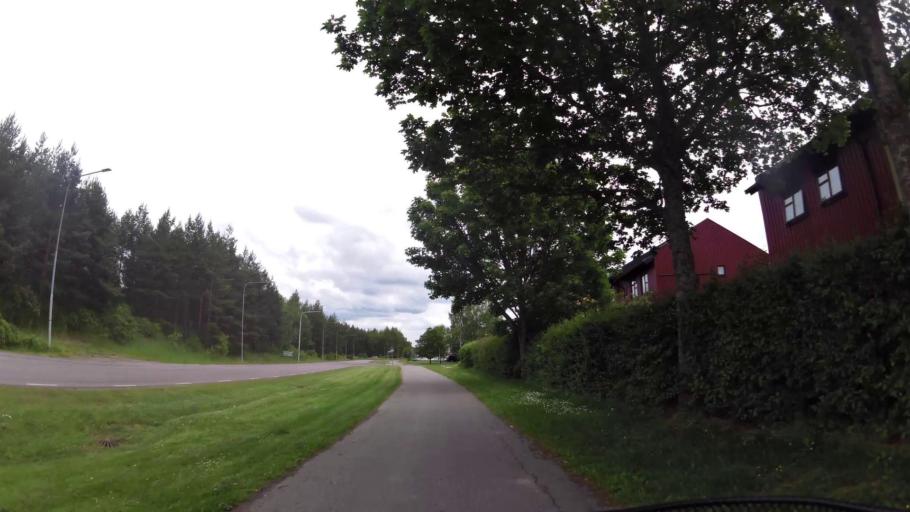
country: SE
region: OEstergoetland
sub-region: Linkopings Kommun
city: Linkoping
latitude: 58.3891
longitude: 15.5733
